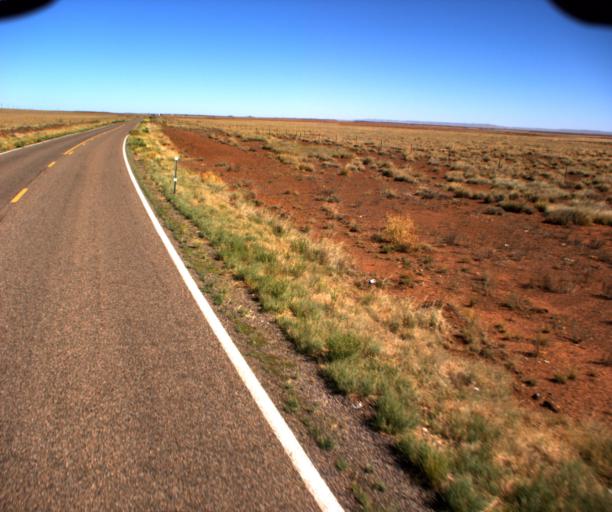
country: US
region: Arizona
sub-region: Coconino County
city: LeChee
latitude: 35.1631
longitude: -110.9116
